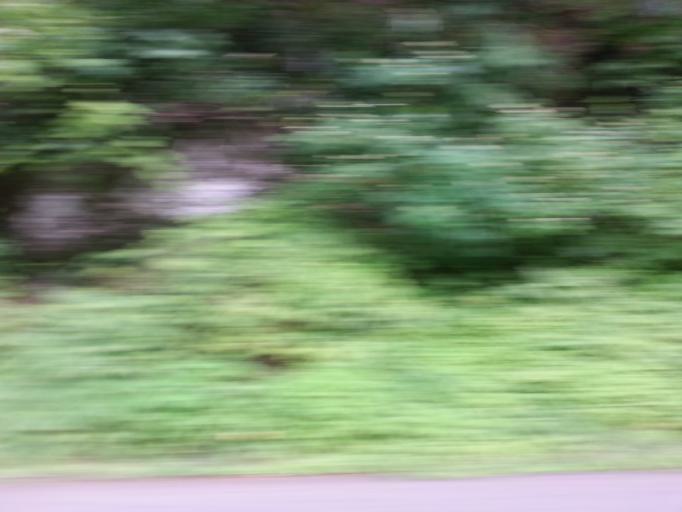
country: US
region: Tennessee
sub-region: Sevier County
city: Pigeon Forge
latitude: 35.6643
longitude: -83.6997
